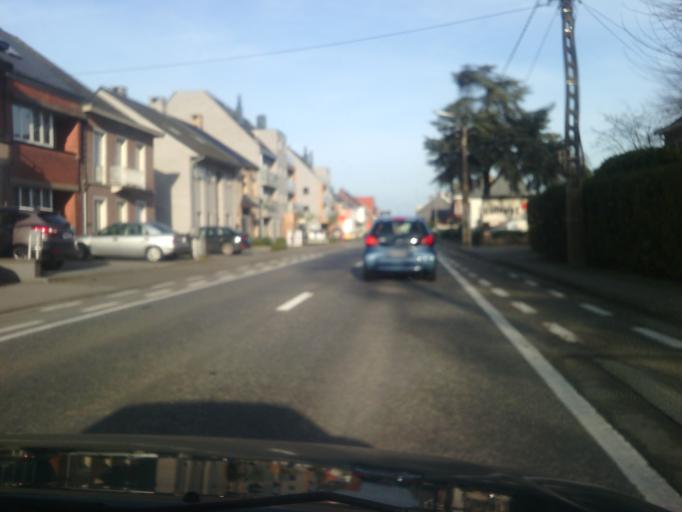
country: BE
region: Flanders
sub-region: Provincie Oost-Vlaanderen
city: Lede
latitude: 50.9626
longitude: 3.9773
